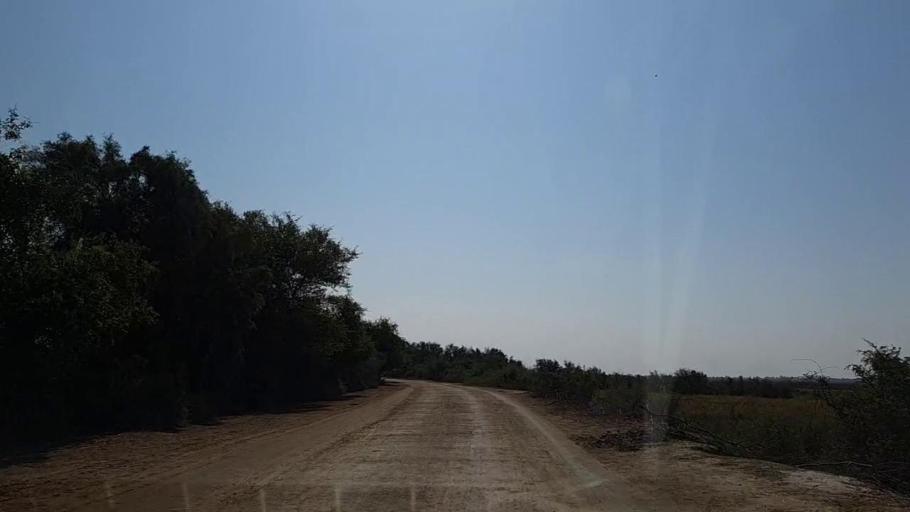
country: PK
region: Sindh
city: Chuhar Jamali
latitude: 24.5143
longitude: 68.0958
